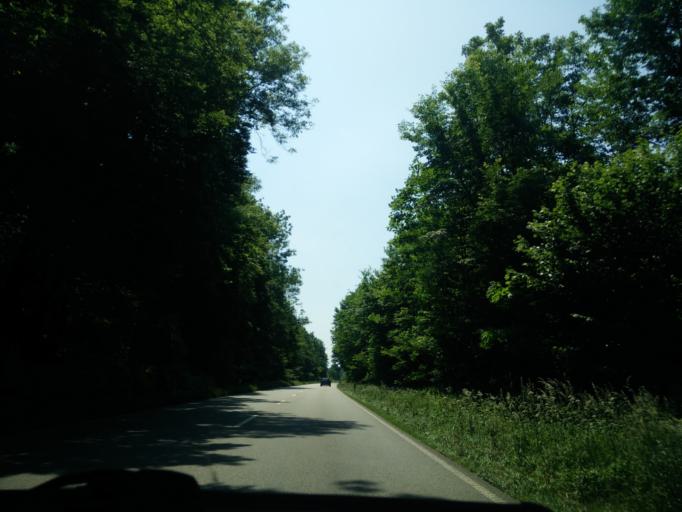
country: DE
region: Bavaria
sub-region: Upper Bavaria
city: Freilassing
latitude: 47.8709
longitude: 12.9754
